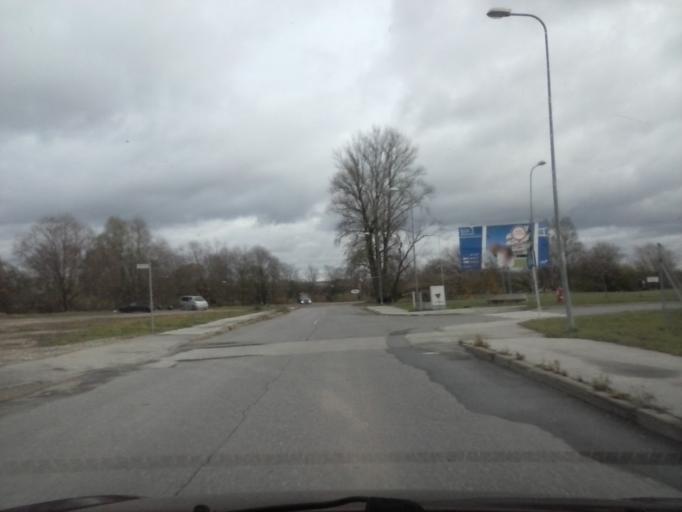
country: EE
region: Tartu
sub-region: Tartu linn
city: Tartu
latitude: 58.3683
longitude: 26.7458
